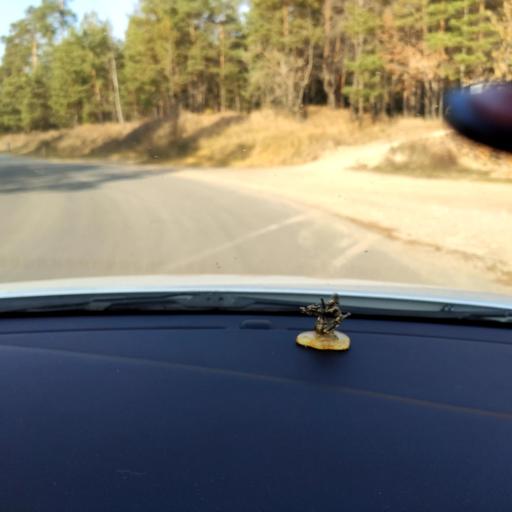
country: RU
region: Tatarstan
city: Staroye Arakchino
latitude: 55.8239
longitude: 48.9176
